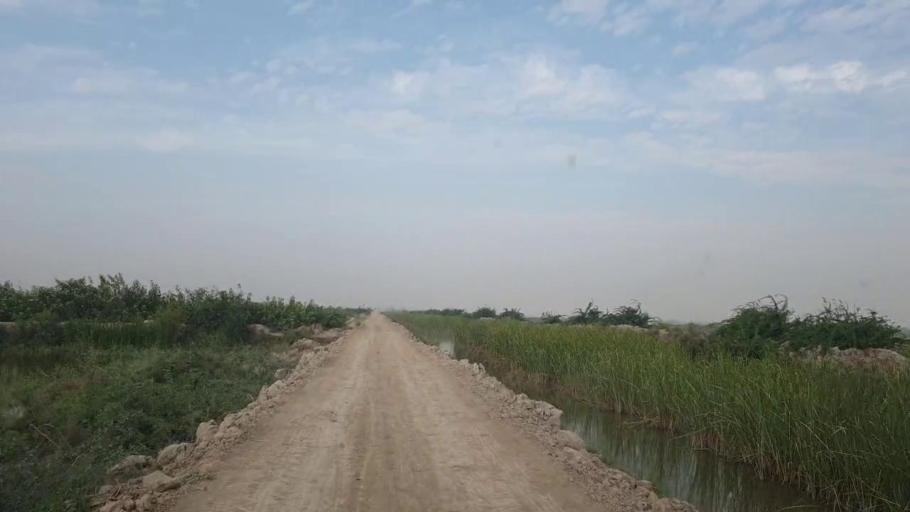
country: PK
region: Sindh
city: Tando Bago
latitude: 24.8657
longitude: 68.9880
